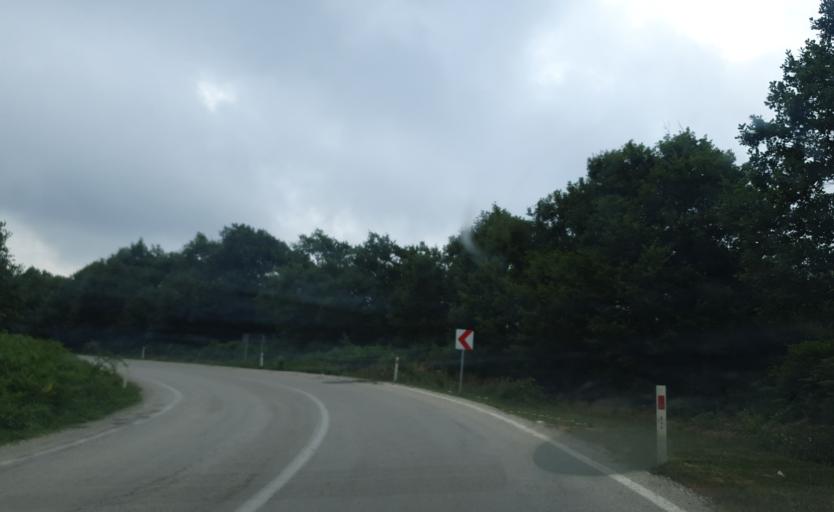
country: TR
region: Kirklareli
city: Salmydessus
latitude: 41.5739
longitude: 28.0792
